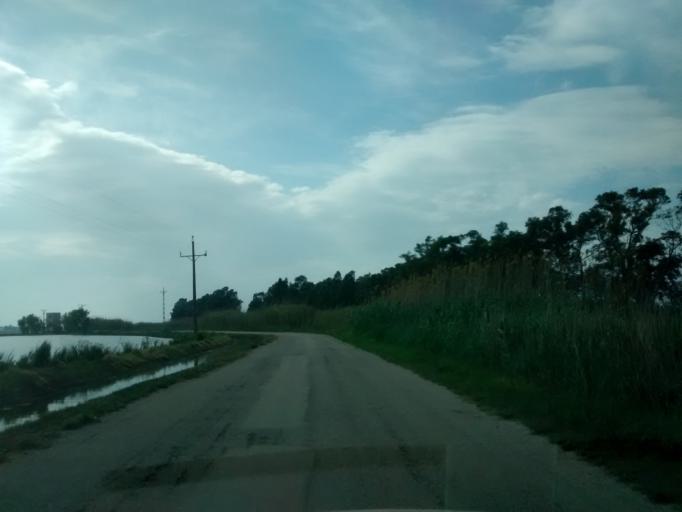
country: ES
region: Catalonia
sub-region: Provincia de Tarragona
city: Deltebre
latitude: 40.6981
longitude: 0.8331
